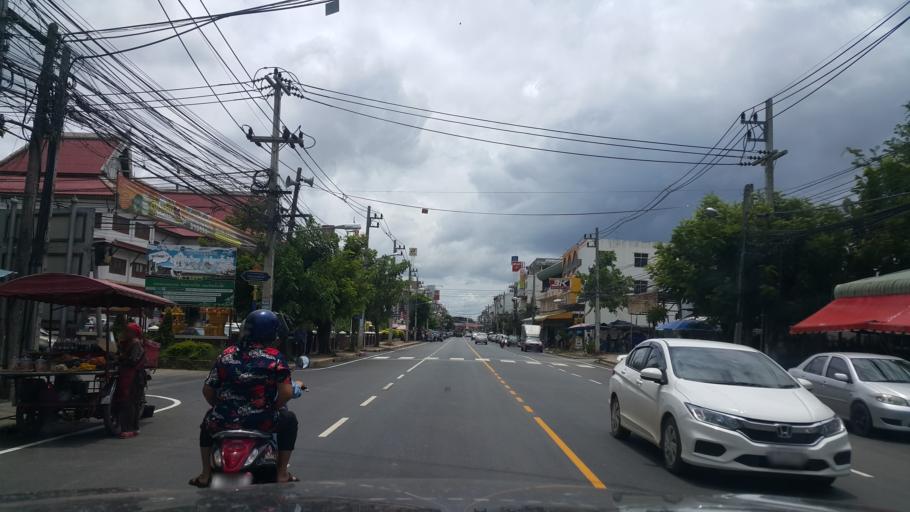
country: TH
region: Sukhothai
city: Sukhothai
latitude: 17.0077
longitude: 99.8240
